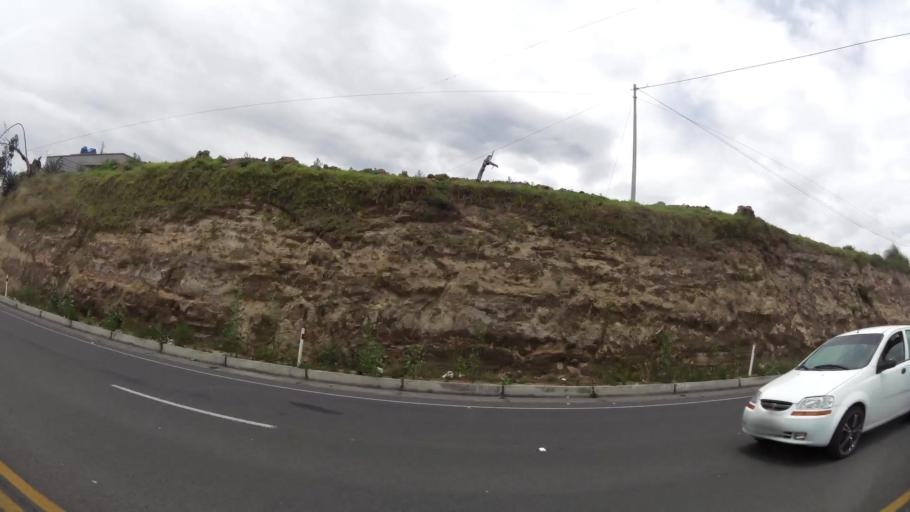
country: EC
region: Cotopaxi
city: San Miguel de Salcedo
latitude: -1.0022
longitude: -78.5935
